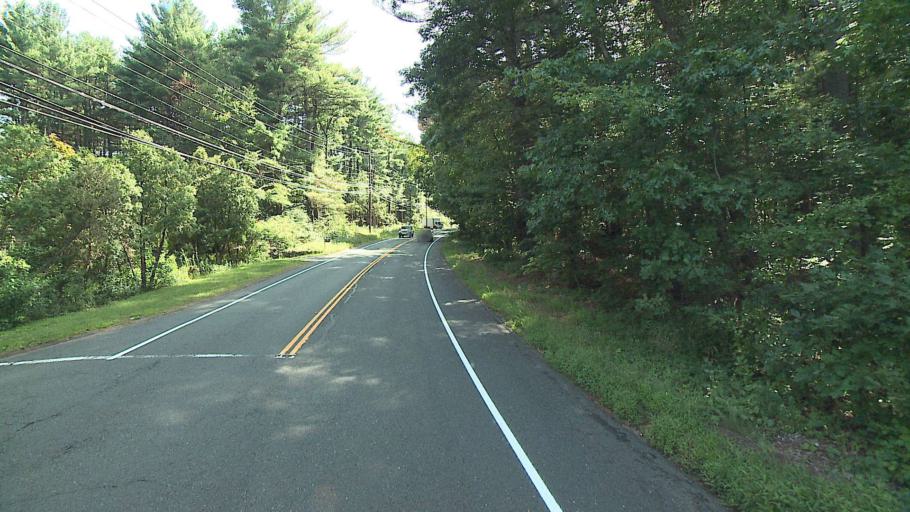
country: US
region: Connecticut
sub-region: Hartford County
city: Weatogue
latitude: 41.8257
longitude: -72.8569
